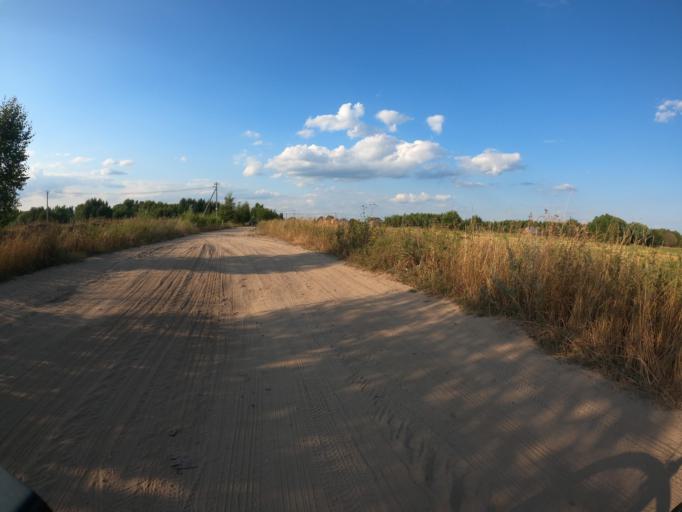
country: RU
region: Moskovskaya
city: Bronnitsy
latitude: 55.4786
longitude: 38.2569
